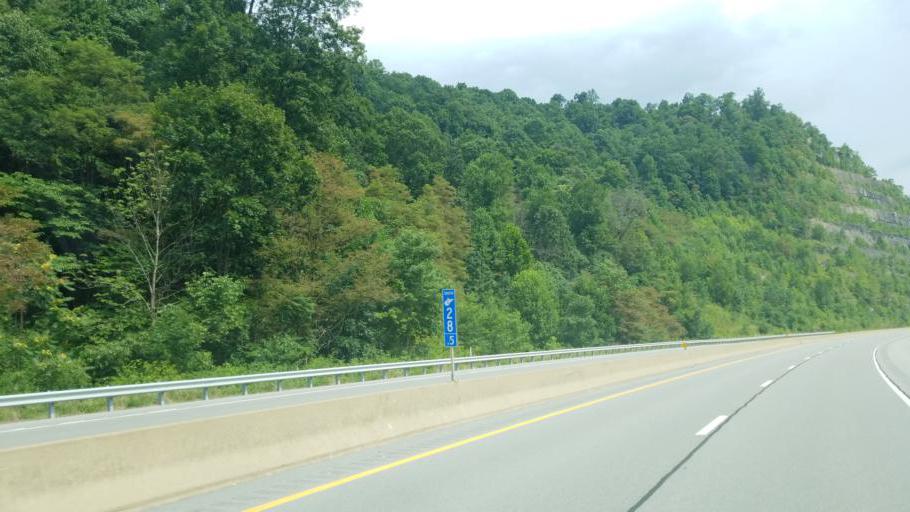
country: US
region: West Virginia
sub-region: Logan County
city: Mount Gay-Shamrock
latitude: 37.8760
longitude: -82.0457
